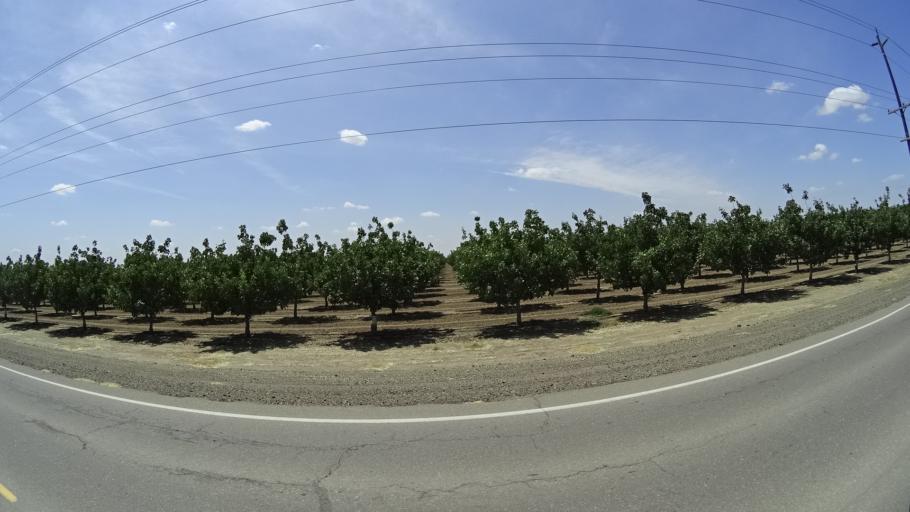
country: US
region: California
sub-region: Kings County
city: Home Garden
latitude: 36.2986
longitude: -119.5591
